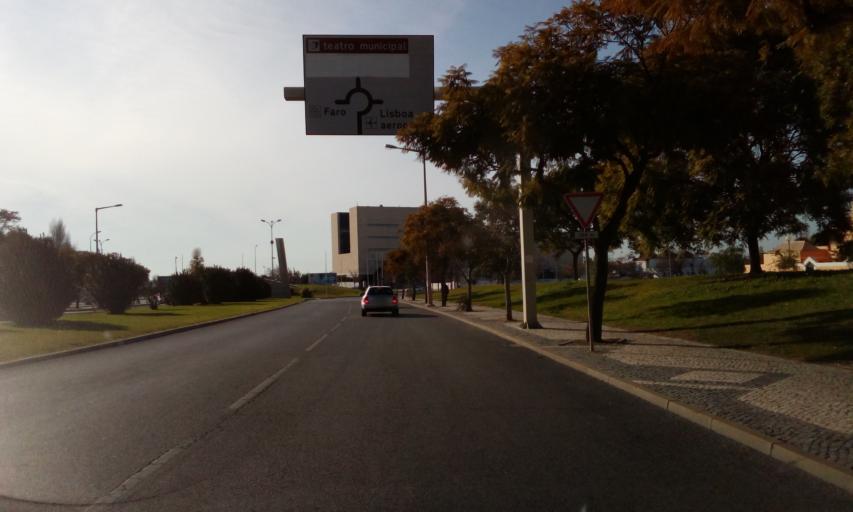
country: PT
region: Faro
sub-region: Faro
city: Faro
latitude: 37.0254
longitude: -7.9418
